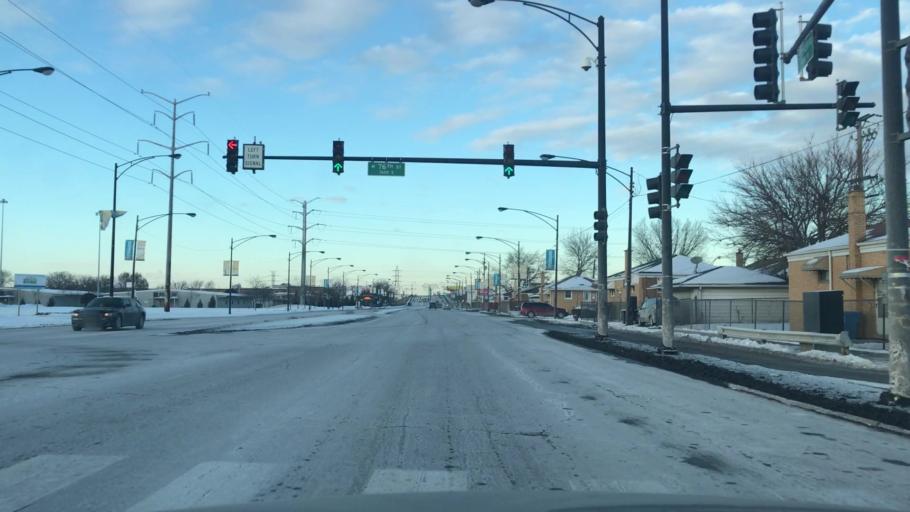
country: US
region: Illinois
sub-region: Cook County
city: Hometown
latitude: 41.7549
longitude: -87.7221
